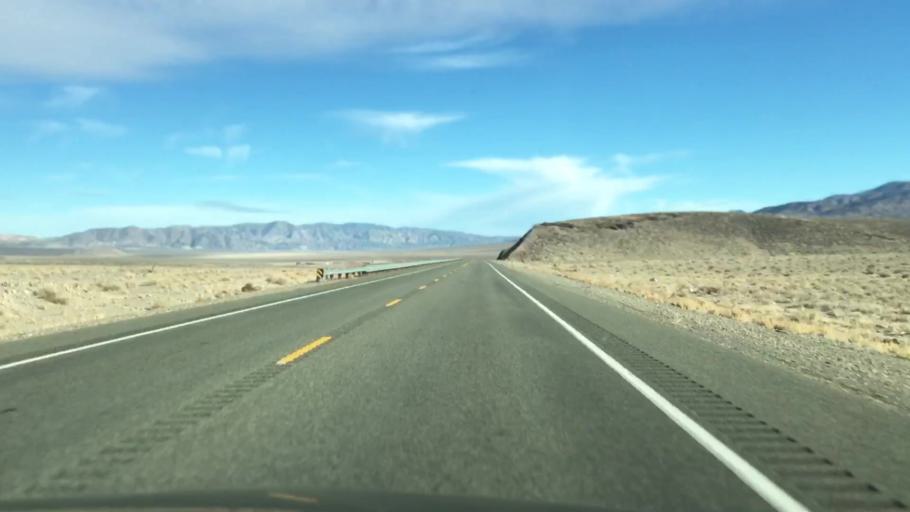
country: US
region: Nevada
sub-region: Mineral County
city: Hawthorne
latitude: 38.5459
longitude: -118.4127
